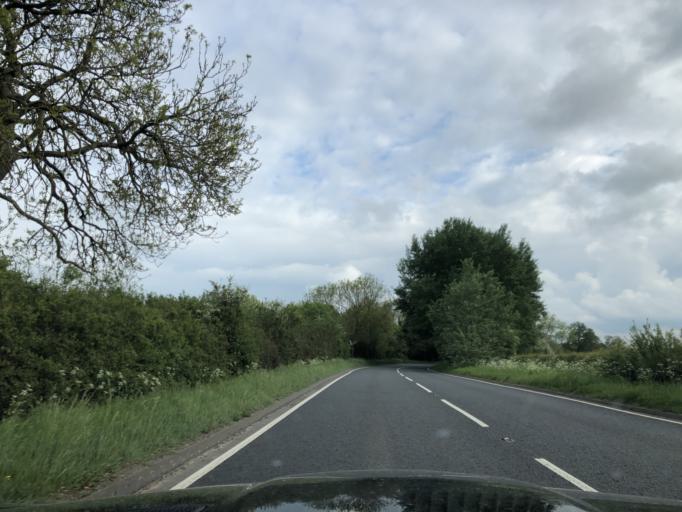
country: GB
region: England
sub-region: Gloucestershire
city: Moreton in Marsh
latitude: 52.0032
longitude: -1.6963
